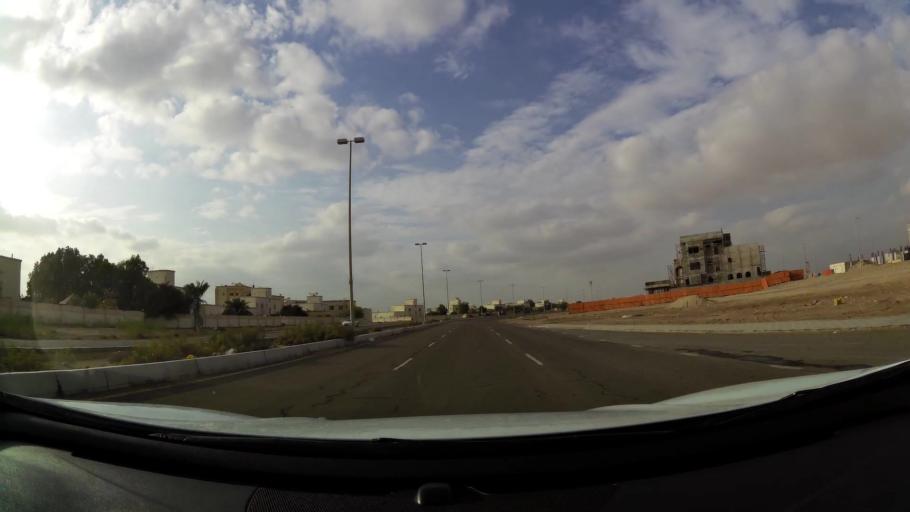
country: AE
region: Abu Dhabi
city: Abu Dhabi
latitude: 24.3434
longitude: 54.5672
